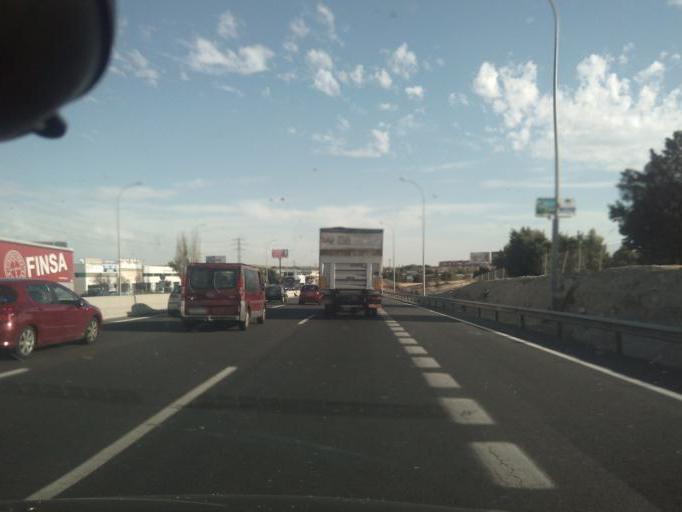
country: ES
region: Madrid
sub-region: Provincia de Madrid
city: Pinto
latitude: 40.2641
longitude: -3.6905
